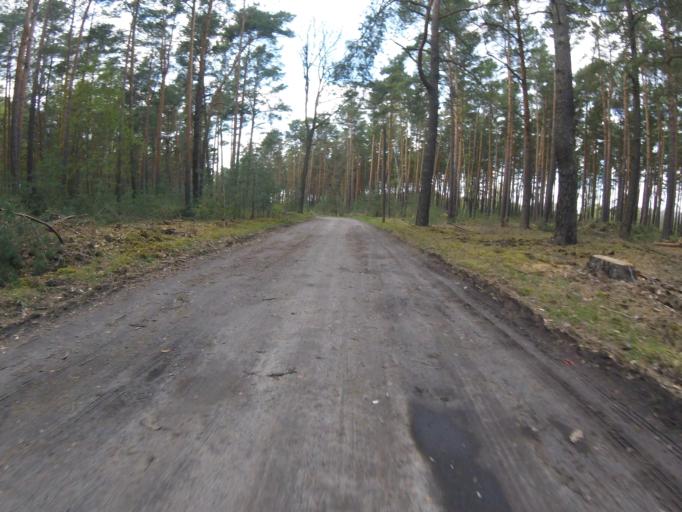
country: DE
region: Brandenburg
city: Munchehofe
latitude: 52.2170
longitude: 13.7689
